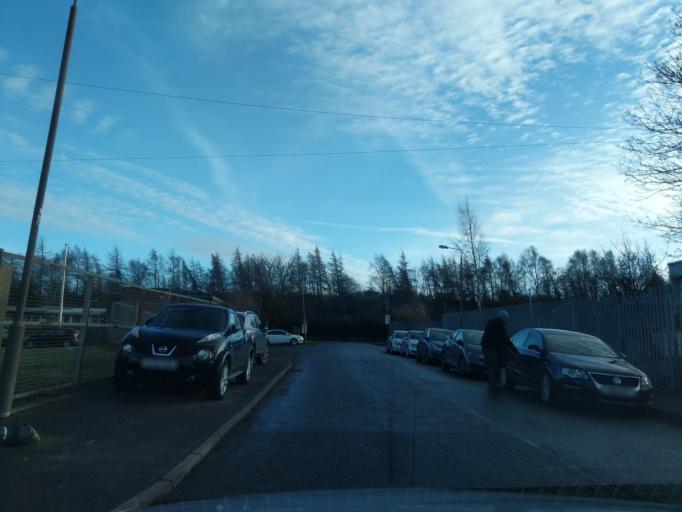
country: GB
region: Scotland
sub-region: Midlothian
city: Loanhead
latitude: 55.8843
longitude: -3.1488
